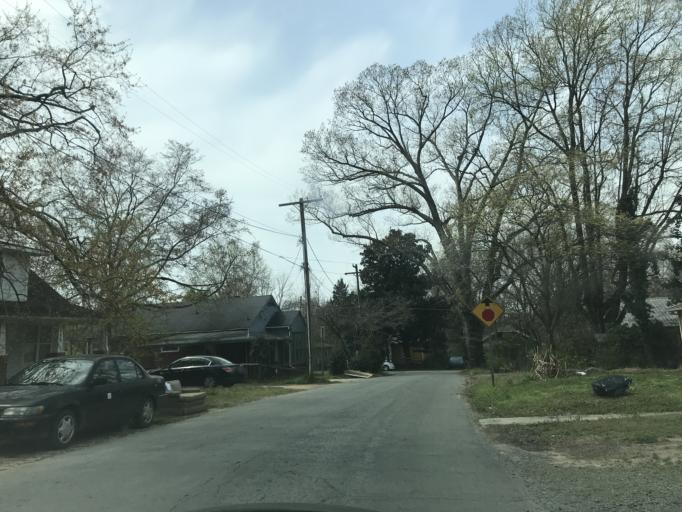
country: US
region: North Carolina
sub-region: Orange County
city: Chapel Hill
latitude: 35.9135
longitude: -79.0658
